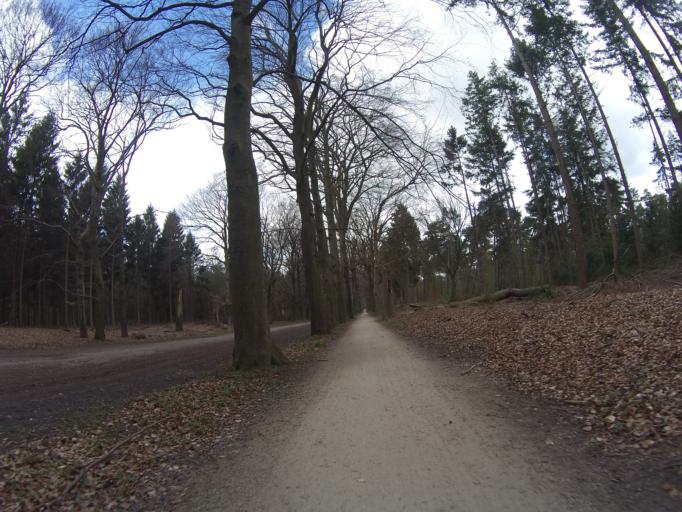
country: NL
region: Utrecht
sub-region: Gemeente Soest
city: Soest
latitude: 52.1807
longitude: 5.2364
